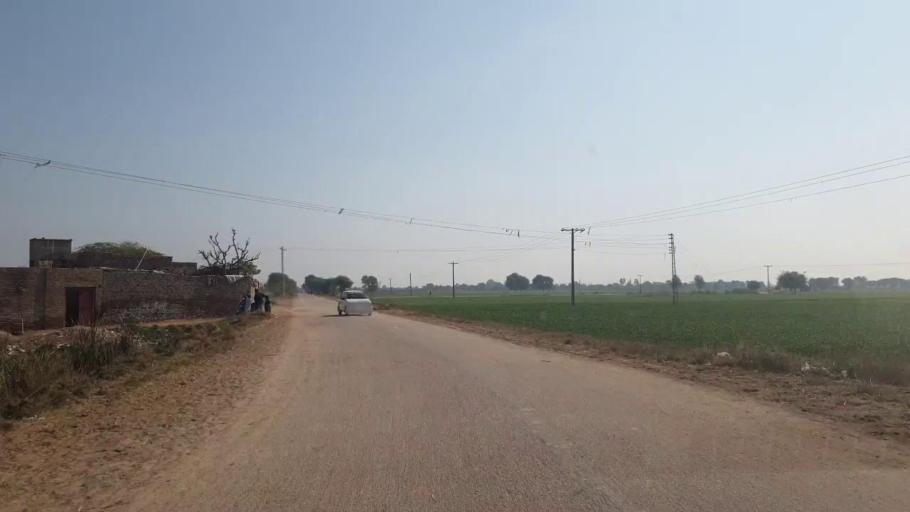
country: PK
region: Sindh
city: Sakrand
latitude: 26.0441
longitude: 68.4217
